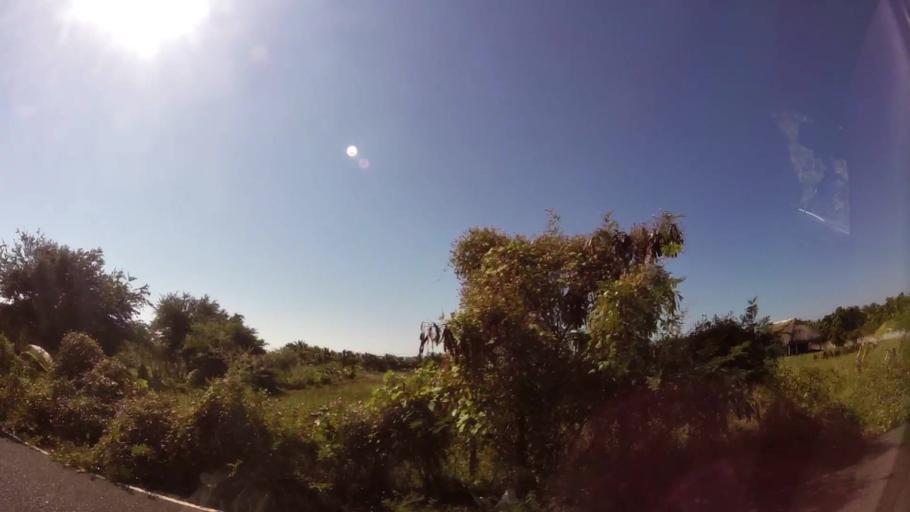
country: GT
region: Santa Rosa
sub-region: Municipio de Taxisco
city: Taxisco
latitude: 13.8834
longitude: -90.4566
